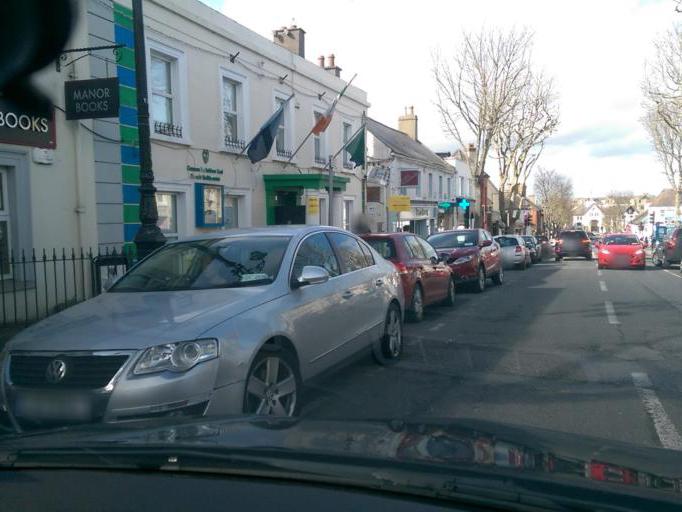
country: IE
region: Leinster
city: Malahide
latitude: 53.4501
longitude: -6.1535
